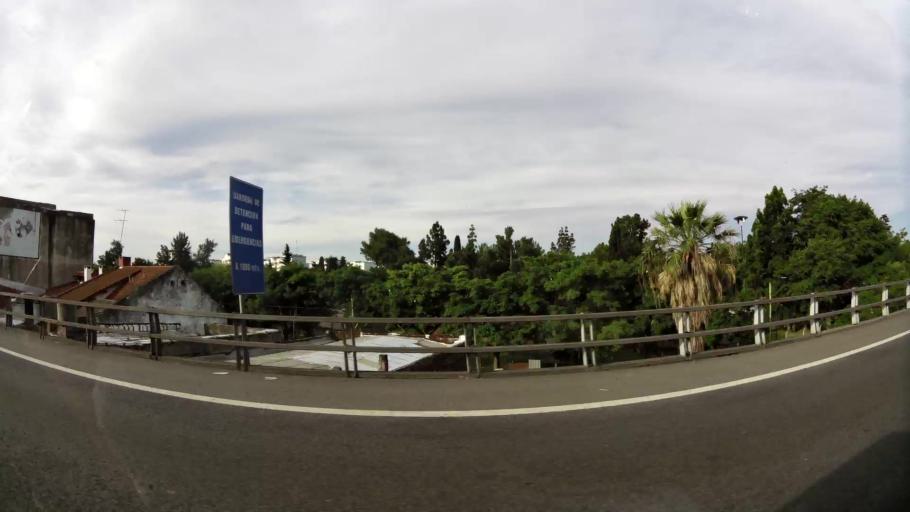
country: AR
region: Buenos Aires F.D.
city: Villa Lugano
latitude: -34.6462
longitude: -58.4837
